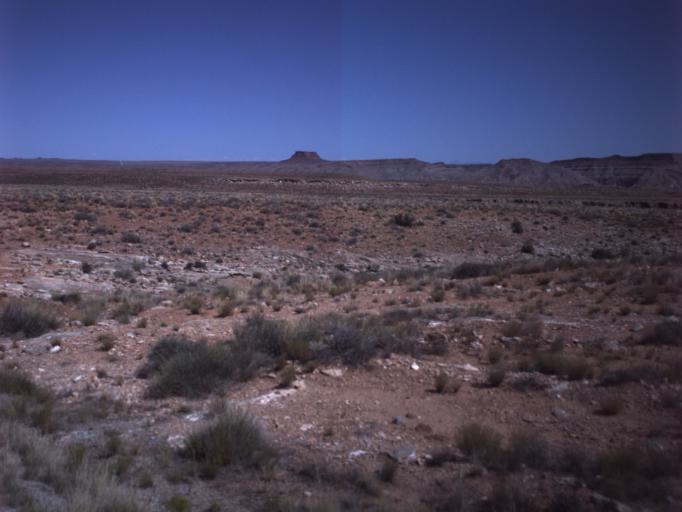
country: US
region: Arizona
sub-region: Navajo County
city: Kayenta
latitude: 37.1845
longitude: -109.9202
